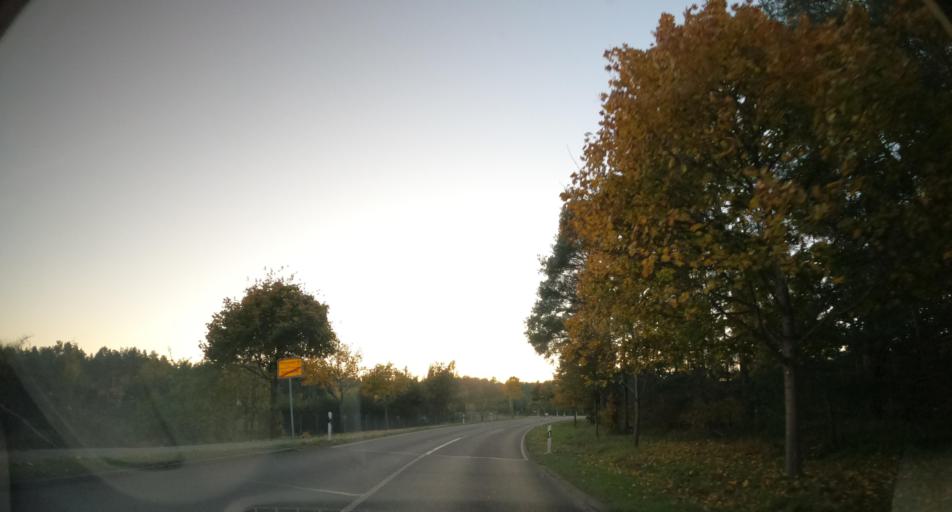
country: DE
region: Mecklenburg-Vorpommern
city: Ueckermunde
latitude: 53.7211
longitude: 14.0761
